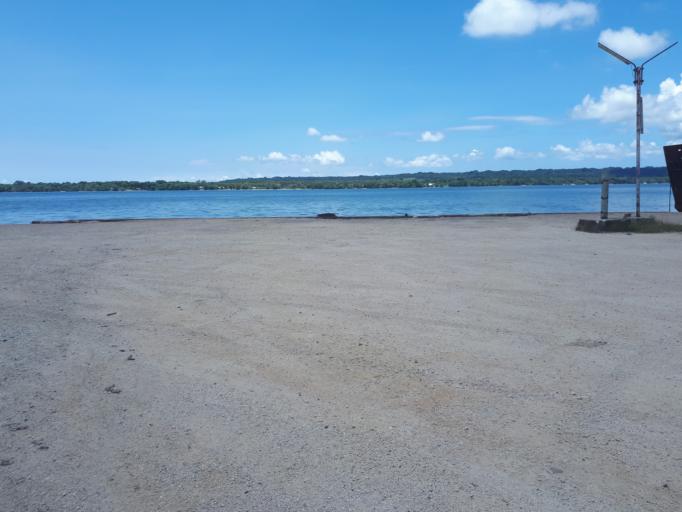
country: VU
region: Sanma
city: Luganville
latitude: -15.5152
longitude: 167.1942
